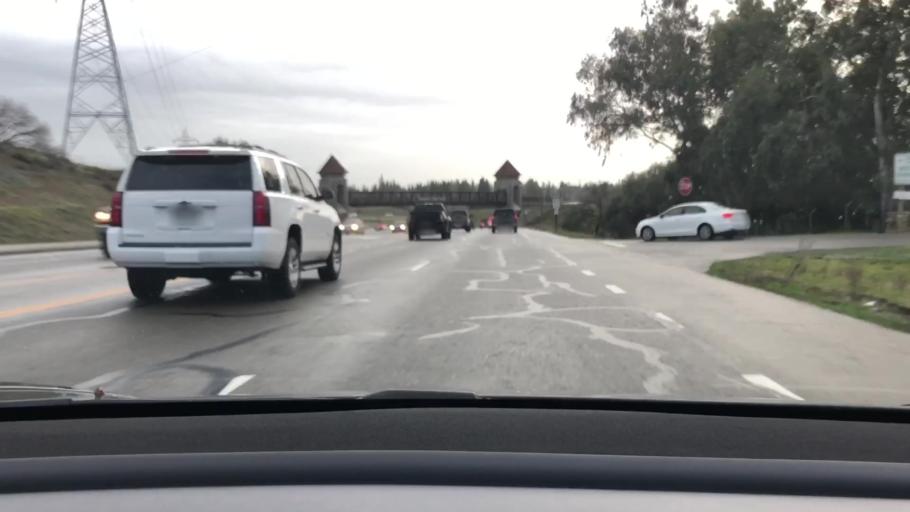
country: US
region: California
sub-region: Sacramento County
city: Folsom
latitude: 38.6976
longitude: -121.1440
